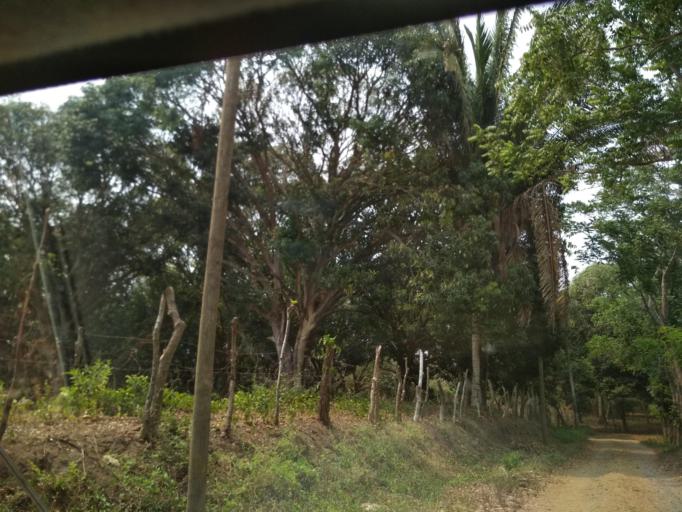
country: MX
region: Veracruz
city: El Tejar
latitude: 19.0586
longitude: -96.1518
